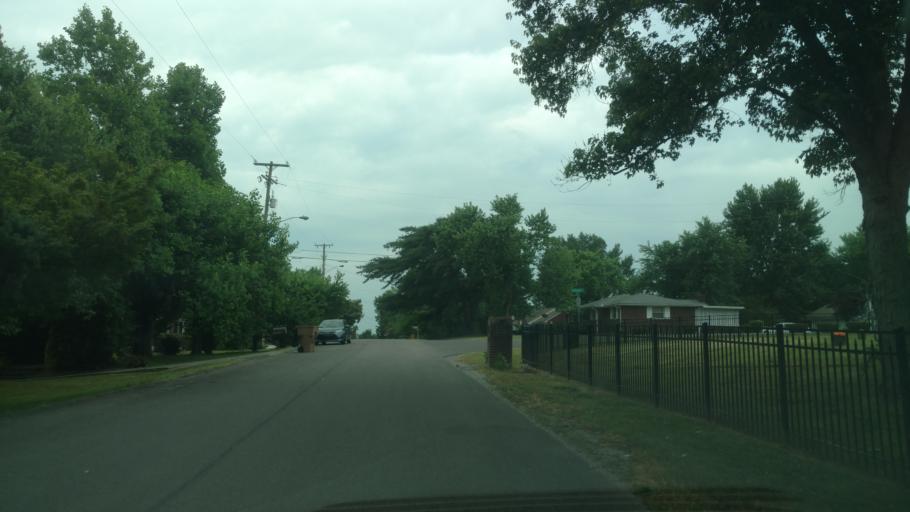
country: US
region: Tennessee
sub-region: Davidson County
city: Lakewood
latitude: 36.2033
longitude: -86.7012
